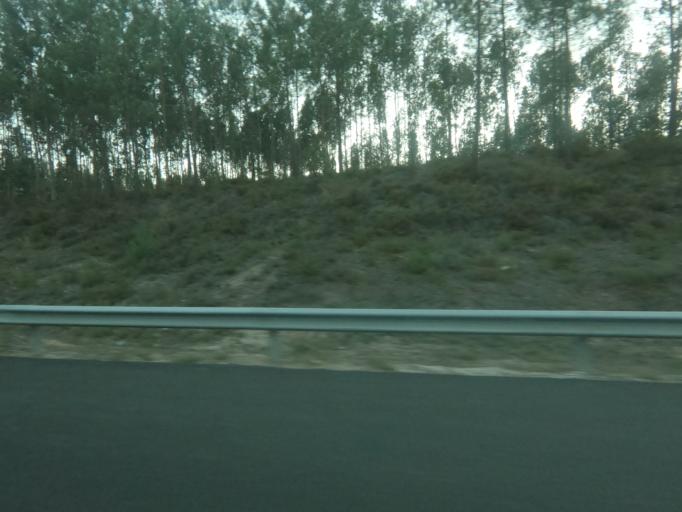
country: PT
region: Leiria
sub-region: Pombal
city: Pombal
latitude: 39.9288
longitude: -8.6801
